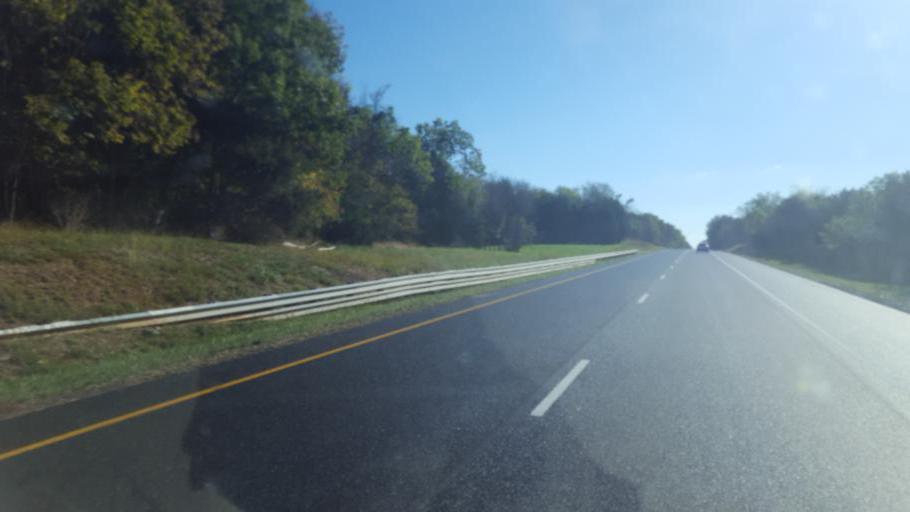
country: US
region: Maryland
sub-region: Washington County
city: Wilson-Conococheague
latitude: 39.6511
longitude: -77.8944
